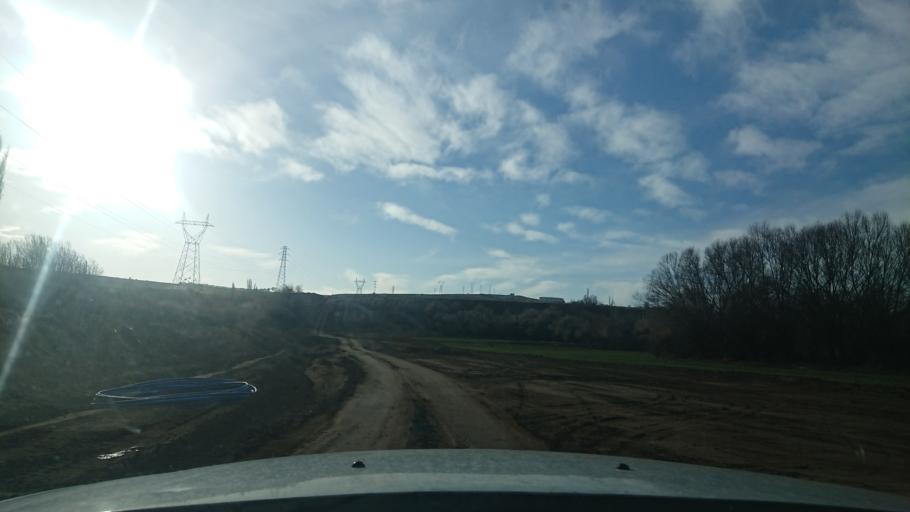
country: TR
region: Aksaray
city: Agacoren
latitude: 38.8606
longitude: 33.9419
